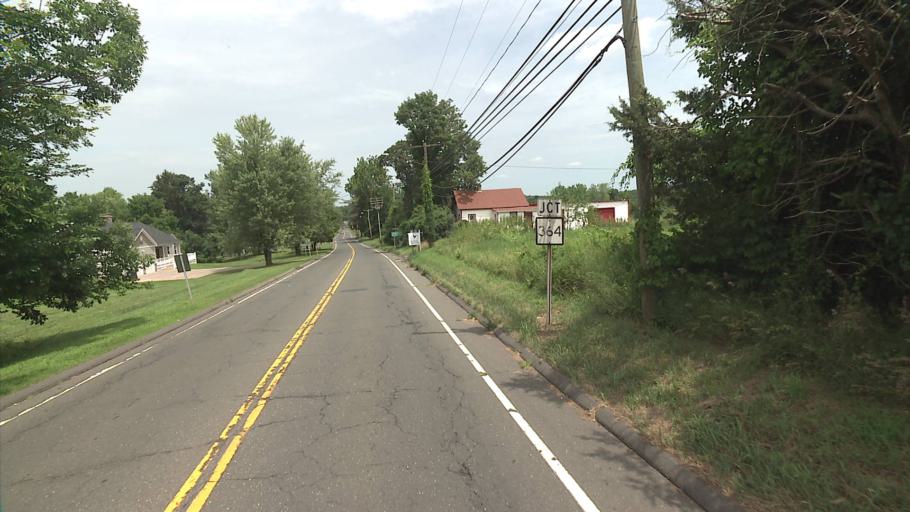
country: US
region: Connecticut
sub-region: Hartford County
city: Kensington
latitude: 41.6012
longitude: -72.7977
